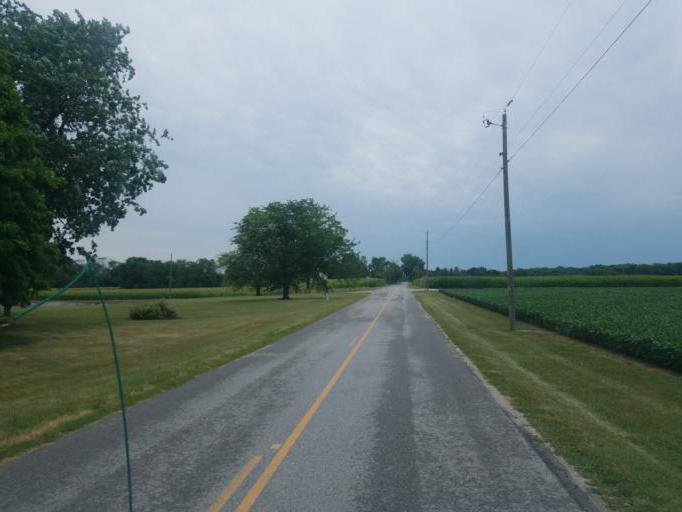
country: US
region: Ohio
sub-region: Paulding County
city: Antwerp
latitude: 41.2374
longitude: -84.7289
